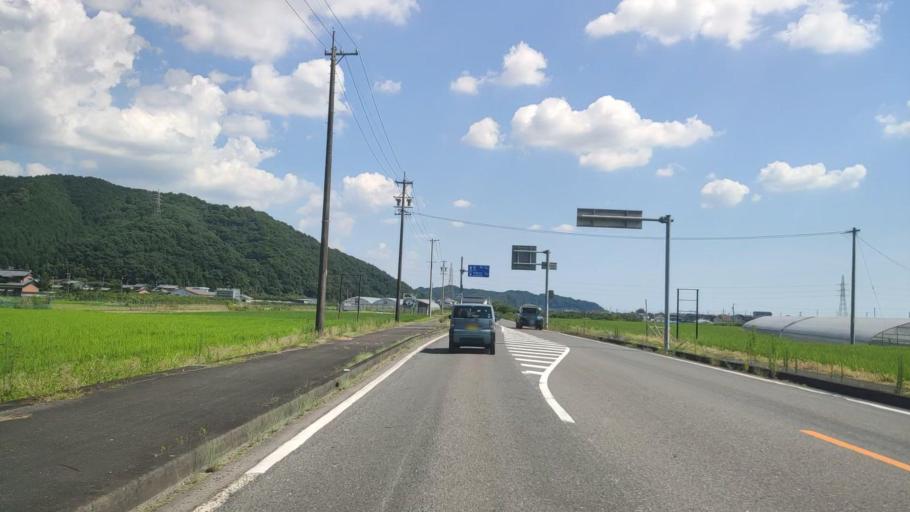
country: JP
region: Gifu
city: Godo
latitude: 35.4980
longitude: 136.6694
